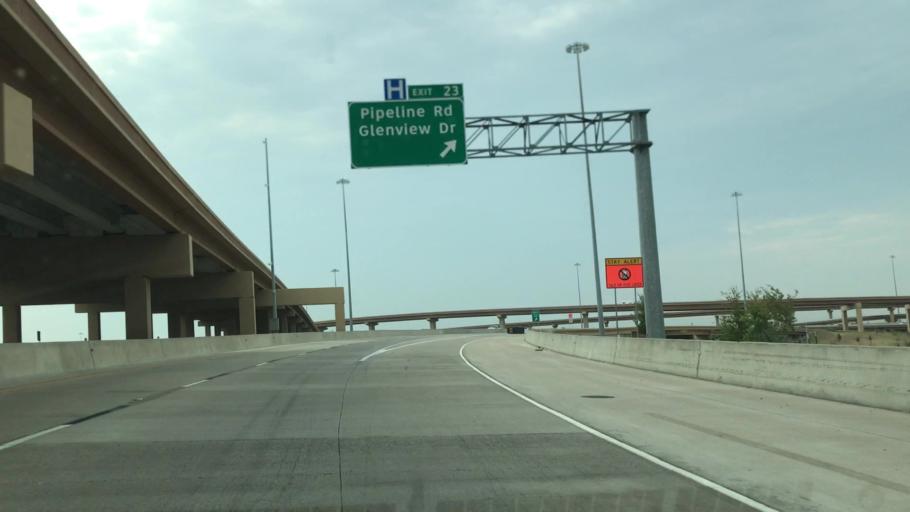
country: US
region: Texas
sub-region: Tarrant County
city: North Richland Hills
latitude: 32.8326
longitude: -97.2098
